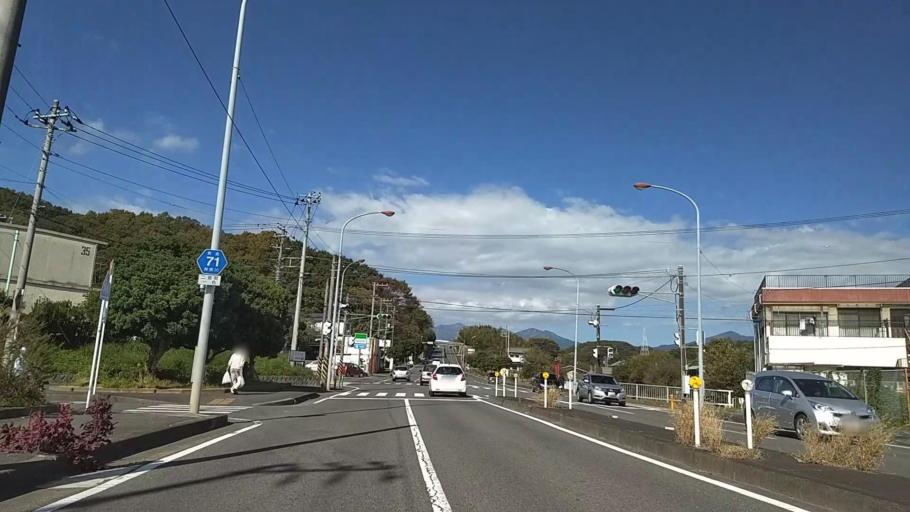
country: JP
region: Kanagawa
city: Ninomiya
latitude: 35.3159
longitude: 139.2423
